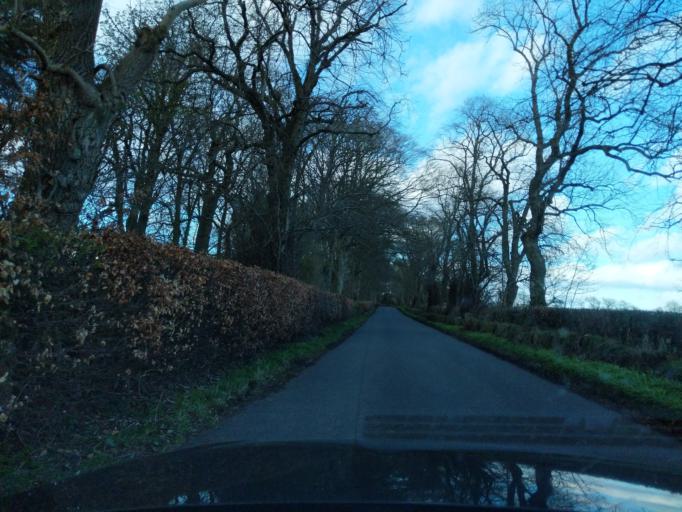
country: GB
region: Scotland
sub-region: Edinburgh
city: Balerno
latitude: 55.8782
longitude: -3.3671
